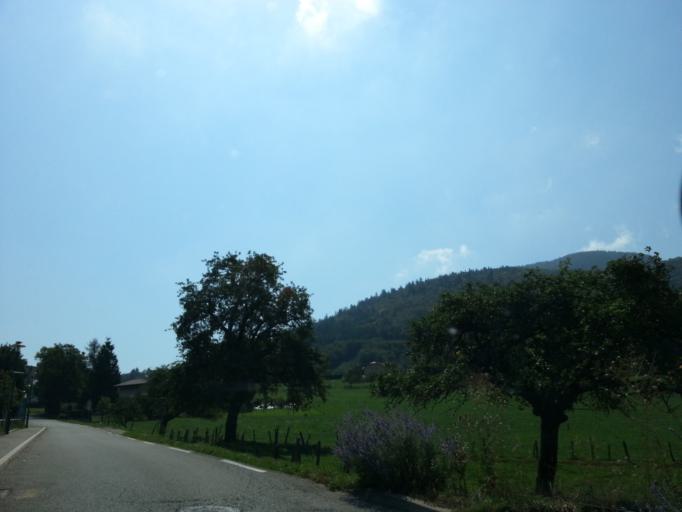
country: FR
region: Rhone-Alpes
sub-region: Departement de la Haute-Savoie
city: Annecy-le-Vieux
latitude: 45.9216
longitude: 6.1698
